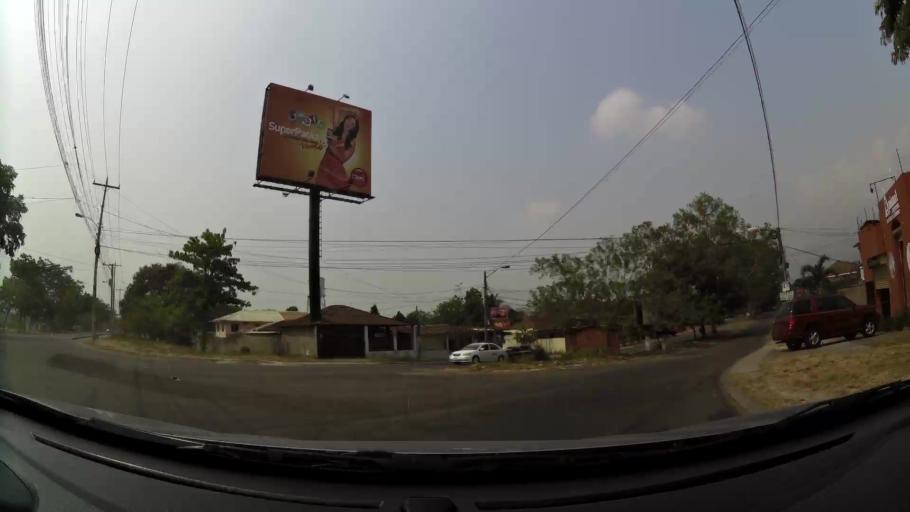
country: HN
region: Cortes
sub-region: San Pedro Sula
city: Pena Blanca
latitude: 15.5585
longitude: -88.0172
